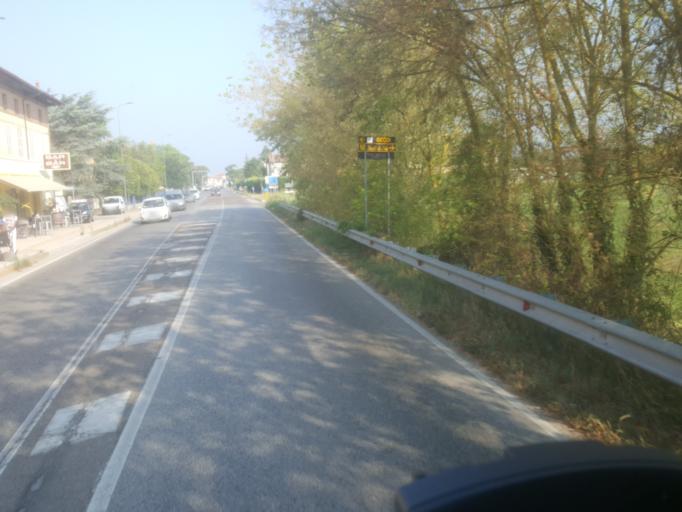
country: IT
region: Emilia-Romagna
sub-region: Provincia di Ravenna
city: Mezzano
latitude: 44.4638
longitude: 12.0919
